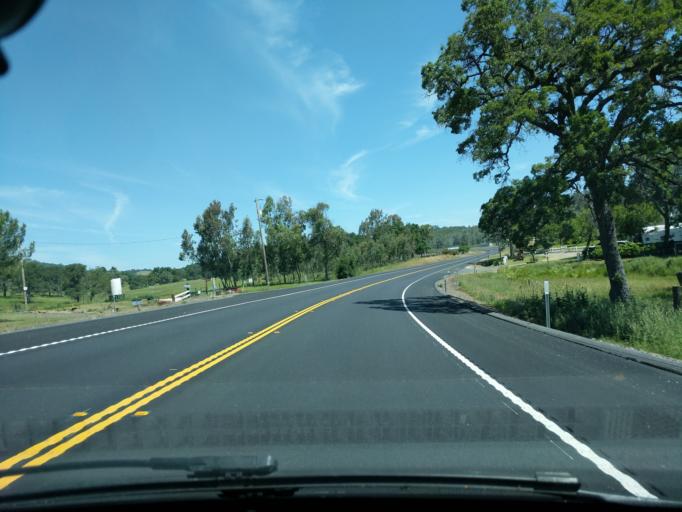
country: US
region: California
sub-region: Calaveras County
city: Copperopolis
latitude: 38.0149
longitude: -120.6445
